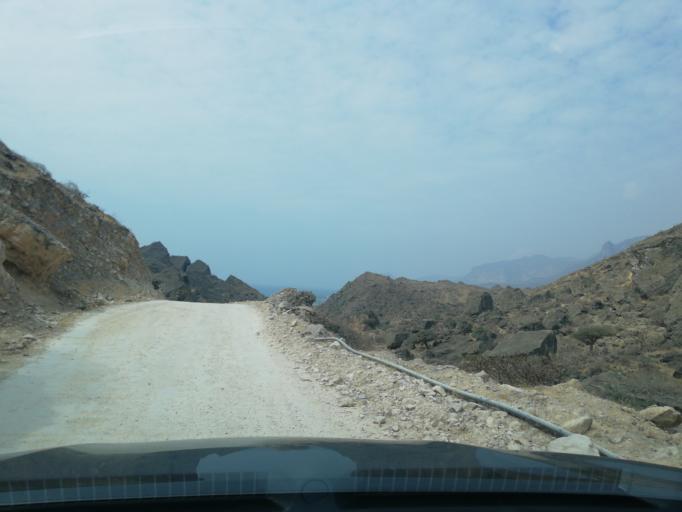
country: OM
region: Zufar
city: Salalah
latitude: 16.8457
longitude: 53.7236
